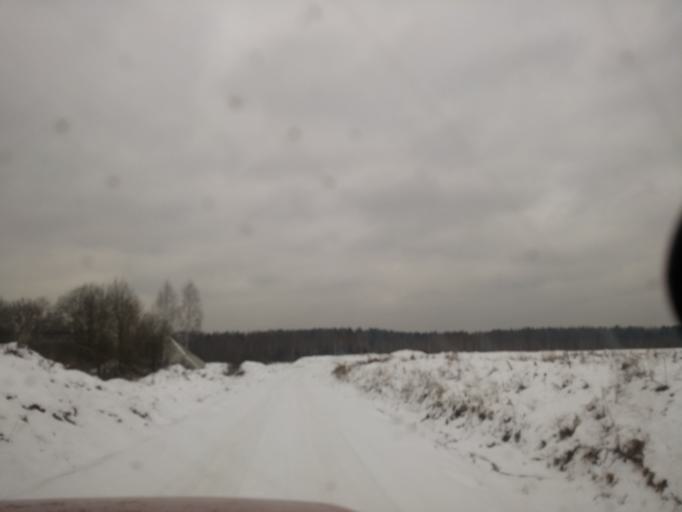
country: RU
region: Moskovskaya
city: Reshetnikovo
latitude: 56.4603
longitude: 36.5435
